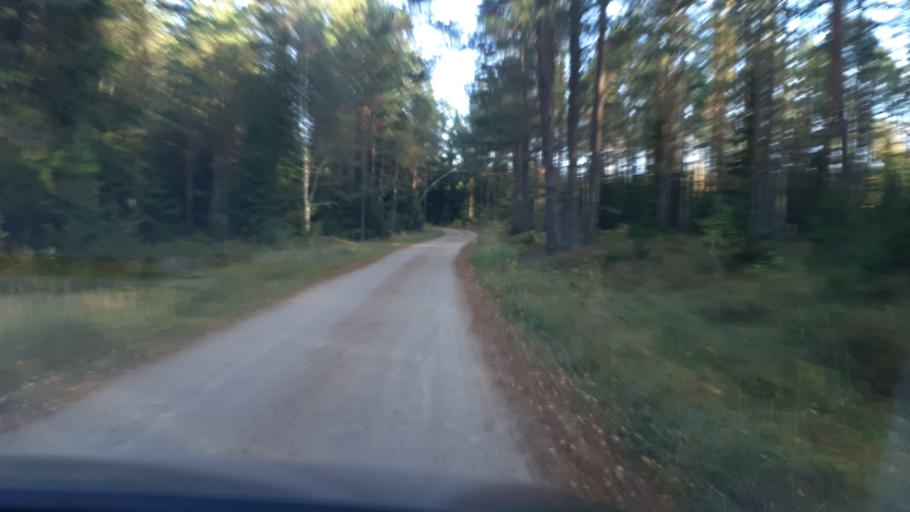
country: LV
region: Kuldigas Rajons
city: Kuldiga
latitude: 56.8590
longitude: 22.1051
